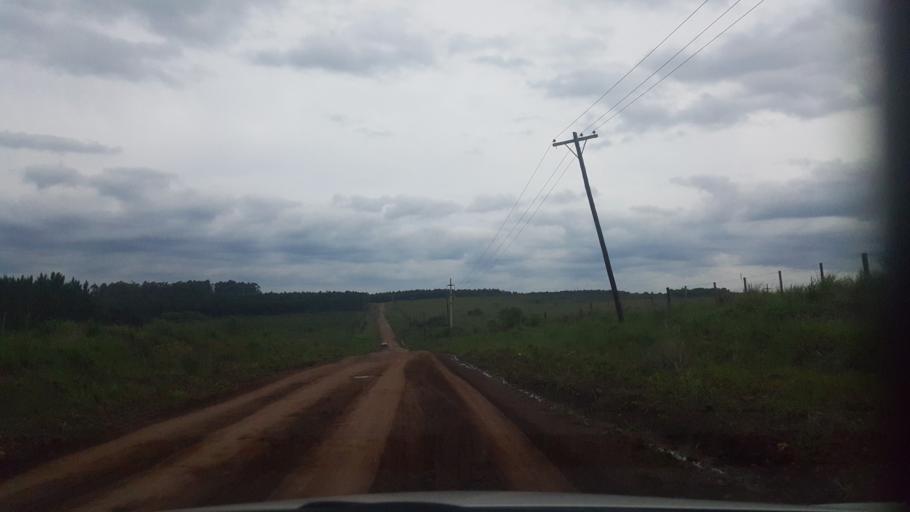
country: AR
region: Misiones
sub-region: Departamento de Candelaria
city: Candelaria
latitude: -27.5021
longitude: -55.7369
